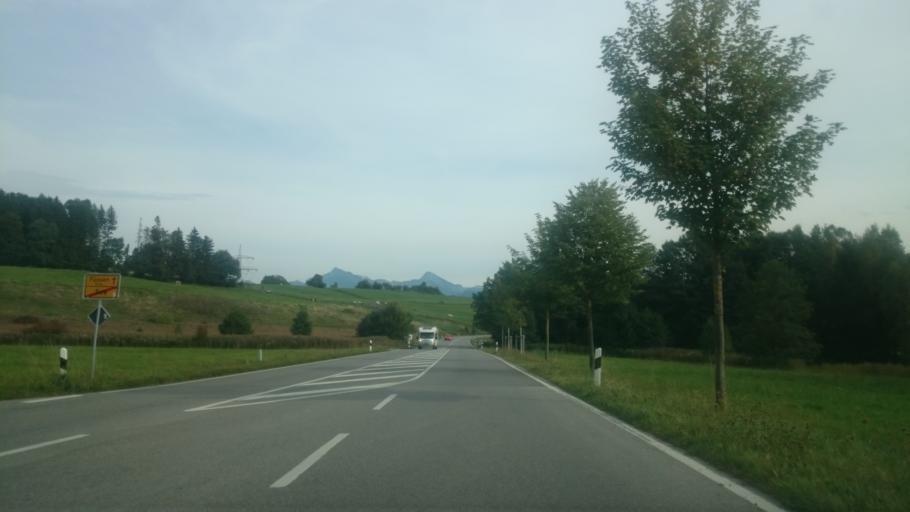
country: AT
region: Tyrol
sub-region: Politischer Bezirk Reutte
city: Vils
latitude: 47.5771
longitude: 10.6301
